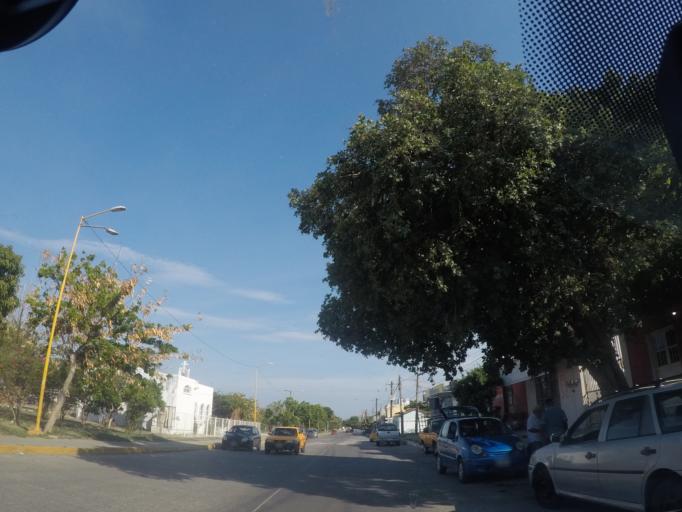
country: MX
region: Oaxaca
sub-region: Salina Cruz
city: Salina Cruz
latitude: 16.1813
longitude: -95.1992
